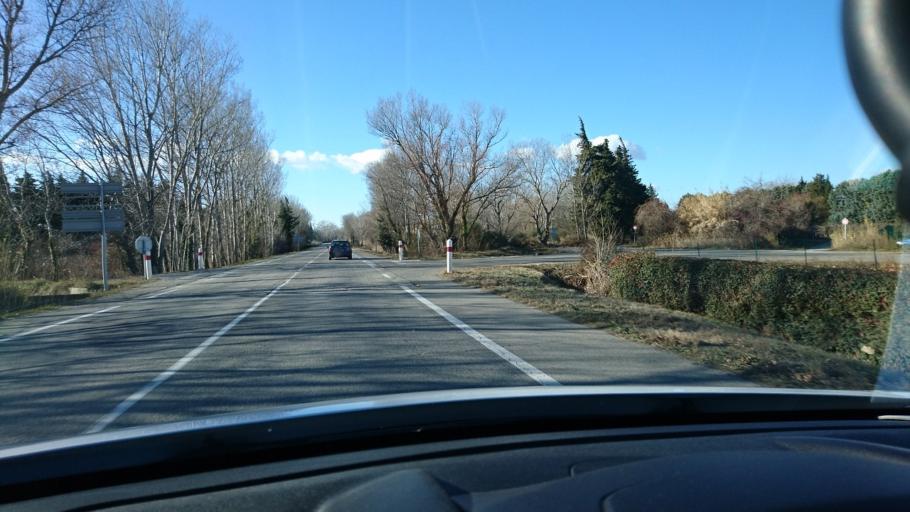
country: FR
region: Provence-Alpes-Cote d'Azur
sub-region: Departement du Vaucluse
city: Caumont-sur-Durance
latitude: 43.8829
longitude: 4.9658
